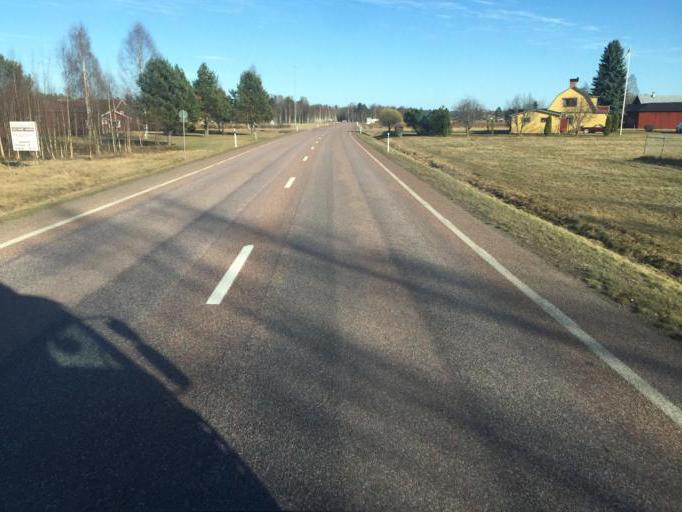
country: SE
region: Dalarna
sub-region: Vansbro Kommun
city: Jarna
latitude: 60.5482
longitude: 14.3711
